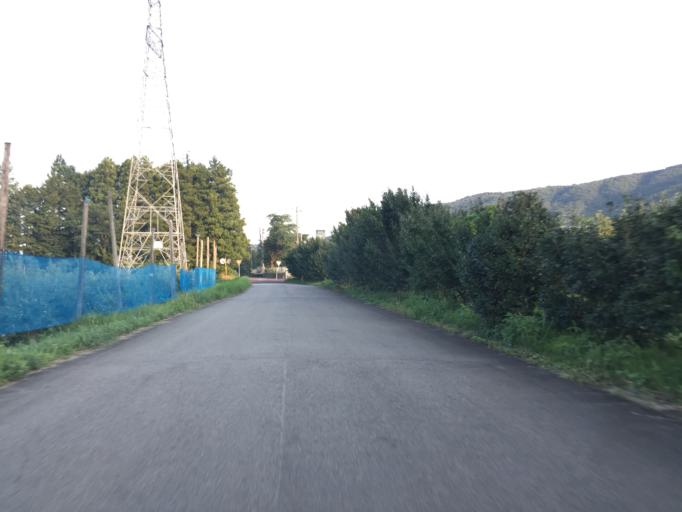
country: JP
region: Fukushima
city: Fukushima-shi
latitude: 37.7124
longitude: 140.3704
